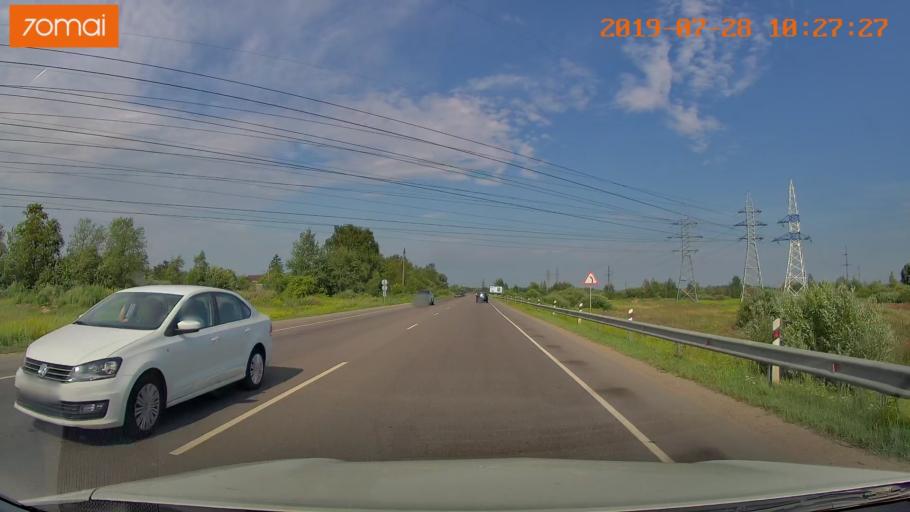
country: RU
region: Kaliningrad
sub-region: Gorod Kaliningrad
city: Kaliningrad
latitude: 54.7707
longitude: 20.5175
